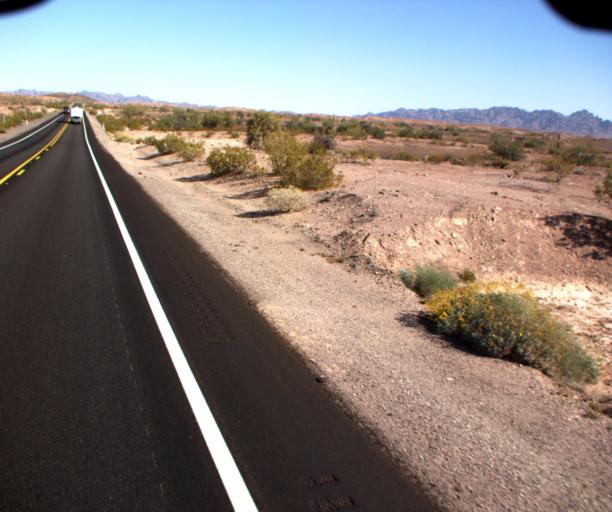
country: US
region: Arizona
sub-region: Yuma County
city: Wellton
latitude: 33.0831
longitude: -114.2960
